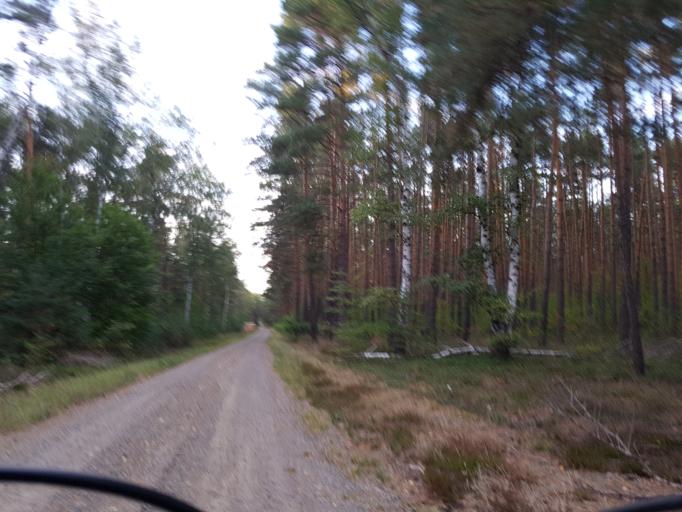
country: DE
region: Brandenburg
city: Schonborn
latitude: 51.5675
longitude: 13.4636
